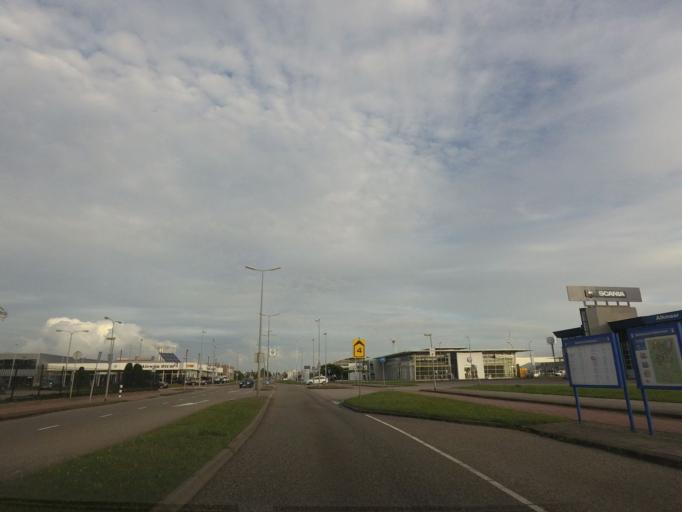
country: NL
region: North Holland
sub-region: Gemeente Alkmaar
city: Alkmaar
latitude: 52.6108
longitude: 4.7473
